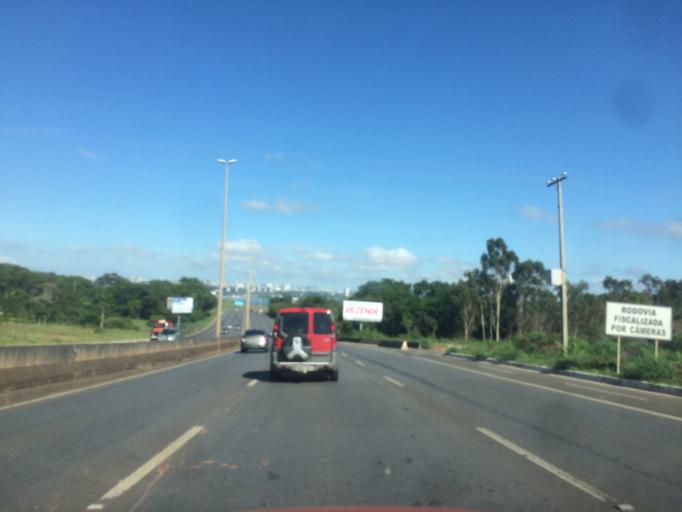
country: BR
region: Federal District
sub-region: Brasilia
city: Brasilia
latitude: -15.8444
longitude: -47.8187
